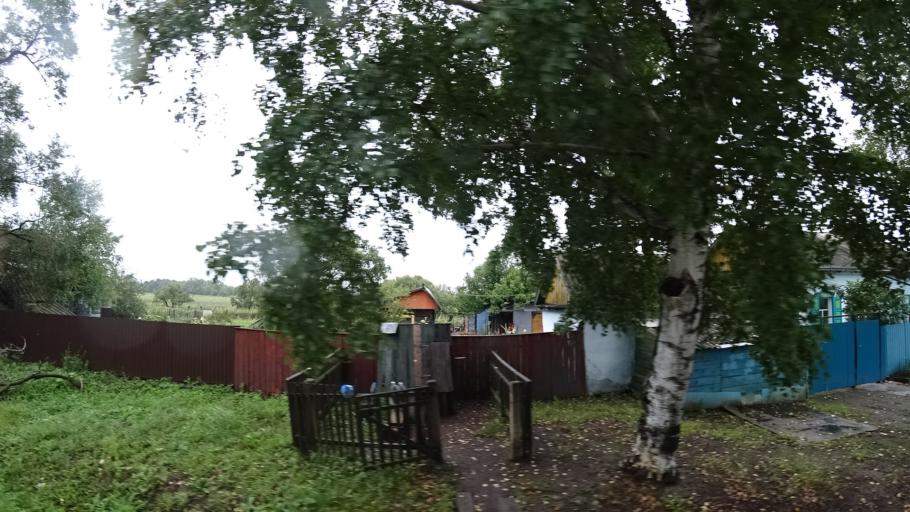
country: RU
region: Primorskiy
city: Monastyrishche
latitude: 44.2014
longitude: 132.4208
